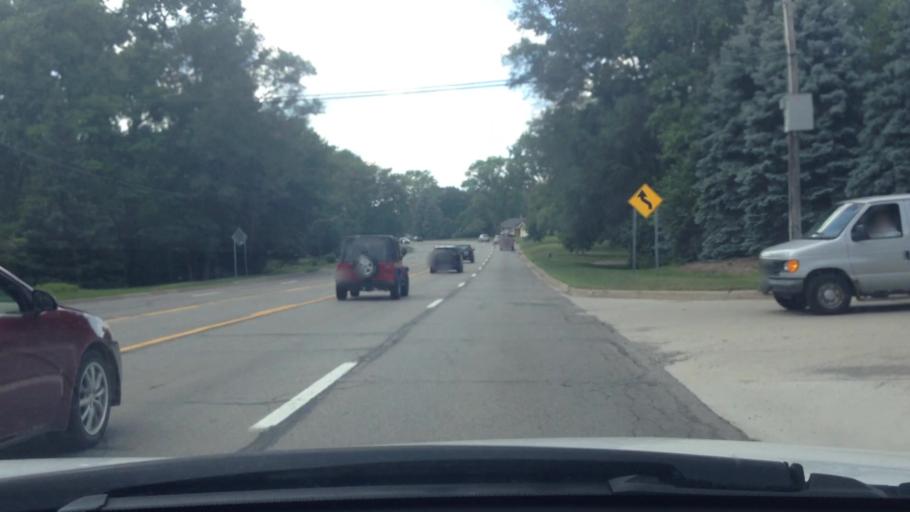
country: US
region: Michigan
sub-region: Oakland County
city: Pontiac
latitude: 42.6815
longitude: -83.3401
